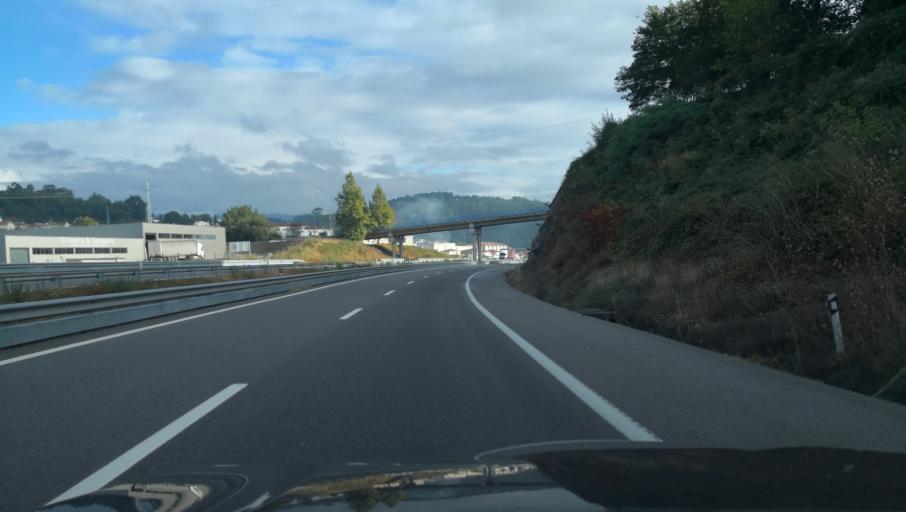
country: PT
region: Braga
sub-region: Guimaraes
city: Candoso
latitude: 41.4189
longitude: -8.3265
